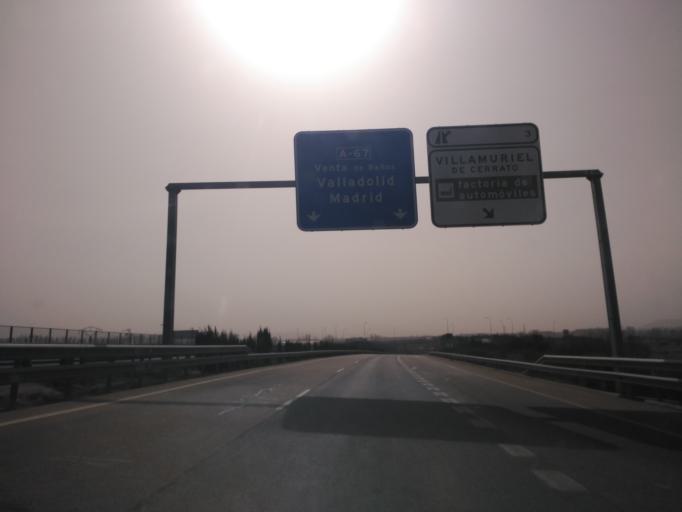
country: ES
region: Castille and Leon
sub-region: Provincia de Palencia
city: Villamuriel de Cerrato
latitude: 41.9583
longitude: -4.5029
